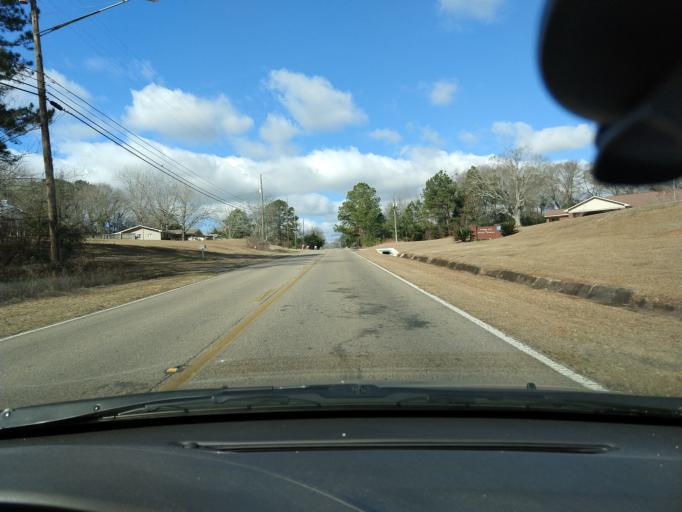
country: US
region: Alabama
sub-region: Coffee County
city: Enterprise
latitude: 31.3228
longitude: -85.8801
